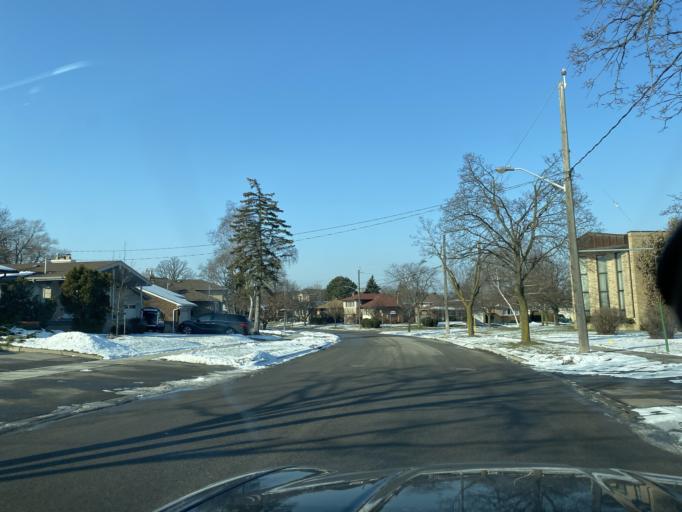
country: CA
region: Ontario
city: Etobicoke
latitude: 43.6576
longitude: -79.5643
